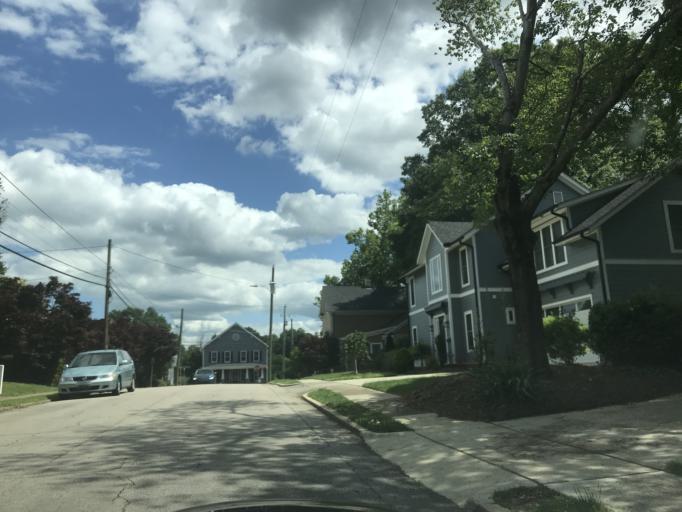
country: US
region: North Carolina
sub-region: Wake County
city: West Raleigh
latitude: 35.8071
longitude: -78.6396
